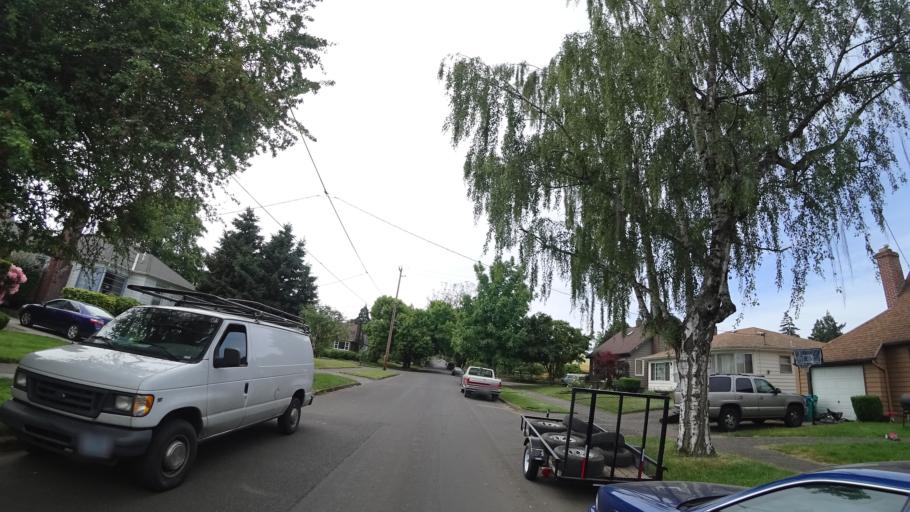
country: US
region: Oregon
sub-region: Multnomah County
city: Portland
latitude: 45.5711
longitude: -122.6425
